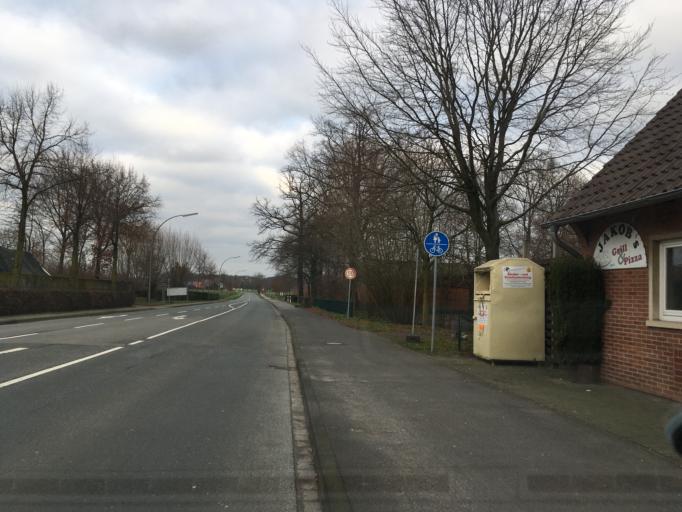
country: DE
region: North Rhine-Westphalia
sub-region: Regierungsbezirk Munster
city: Ahaus
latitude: 52.1244
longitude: 6.9887
